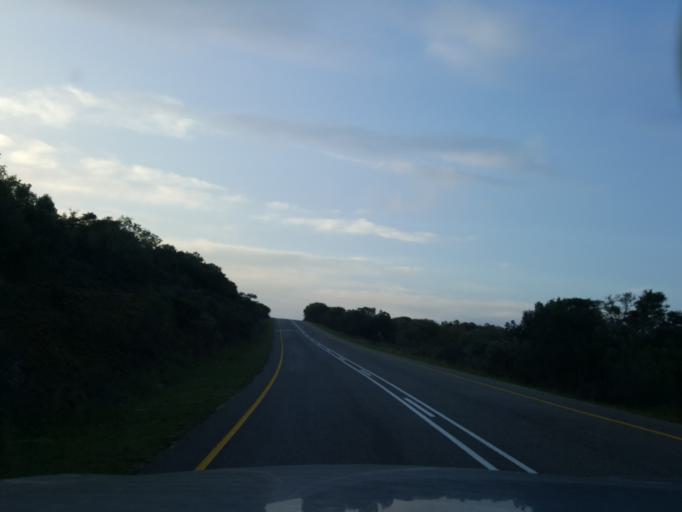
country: ZA
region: Eastern Cape
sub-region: Cacadu District Municipality
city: Grahamstown
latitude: -33.4982
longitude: 26.4858
